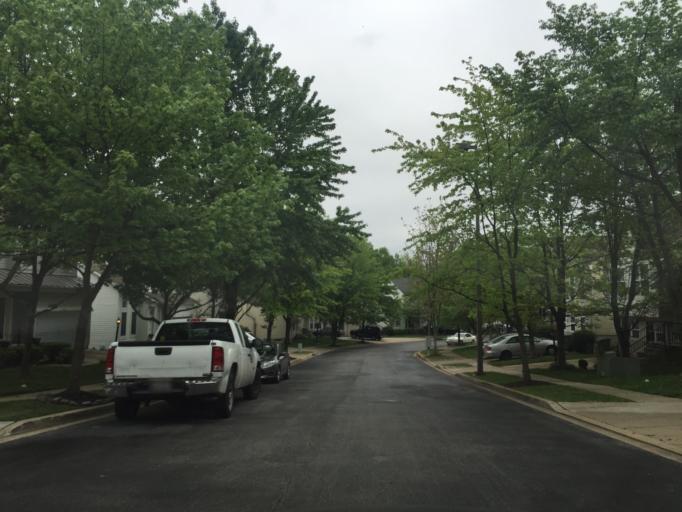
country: US
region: Maryland
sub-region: Baltimore County
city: Lochearn
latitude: 39.3503
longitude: -76.6554
